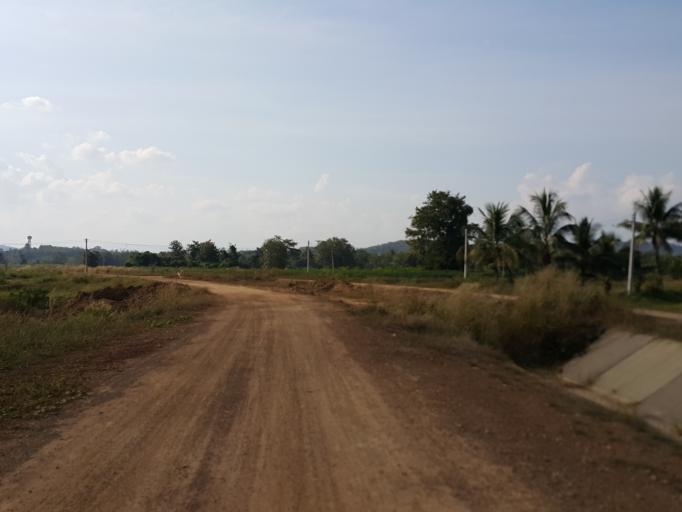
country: TH
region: Sukhothai
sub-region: Amphoe Si Satchanalai
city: Si Satchanalai
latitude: 17.4850
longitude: 99.6465
